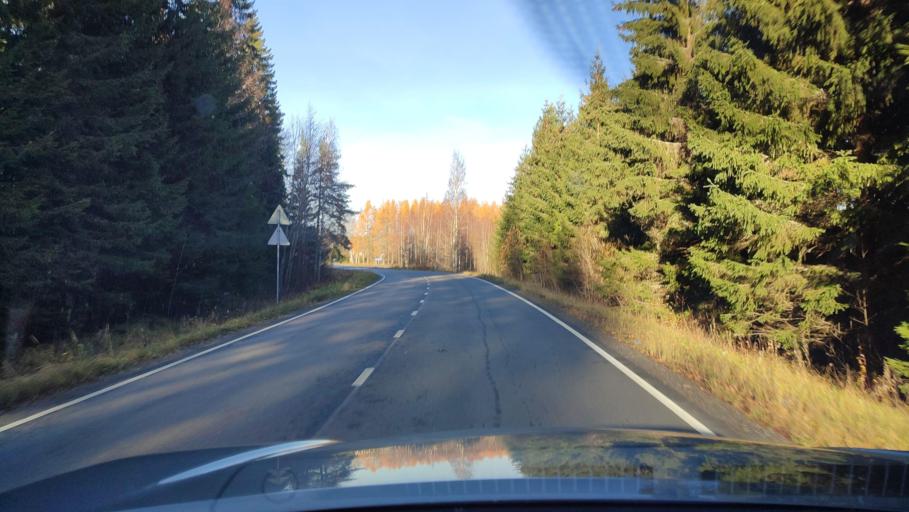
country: FI
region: Southern Ostrobothnia
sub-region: Suupohja
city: Karijoki
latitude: 62.3123
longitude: 21.7037
